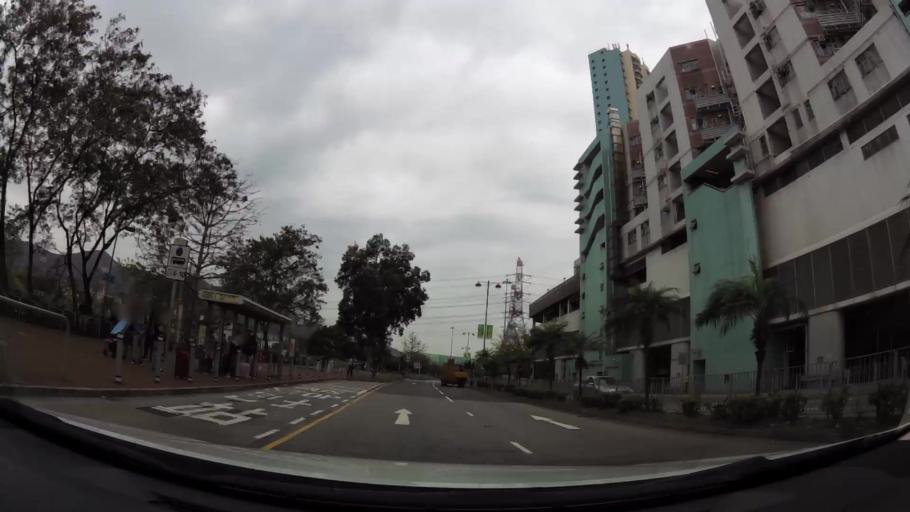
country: HK
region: Tuen Mun
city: Tuen Mun
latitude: 22.4131
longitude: 113.9823
